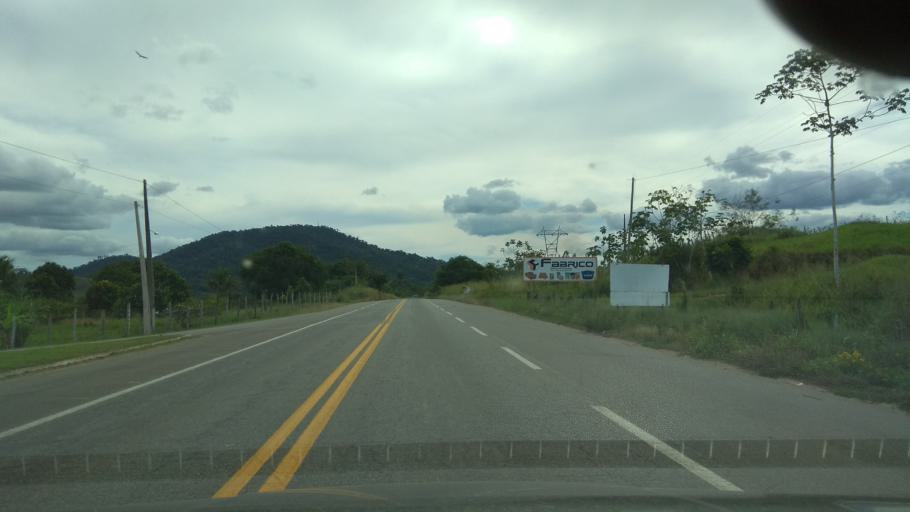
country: BR
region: Bahia
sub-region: Ipiau
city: Ipiau
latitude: -14.1748
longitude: -39.6777
